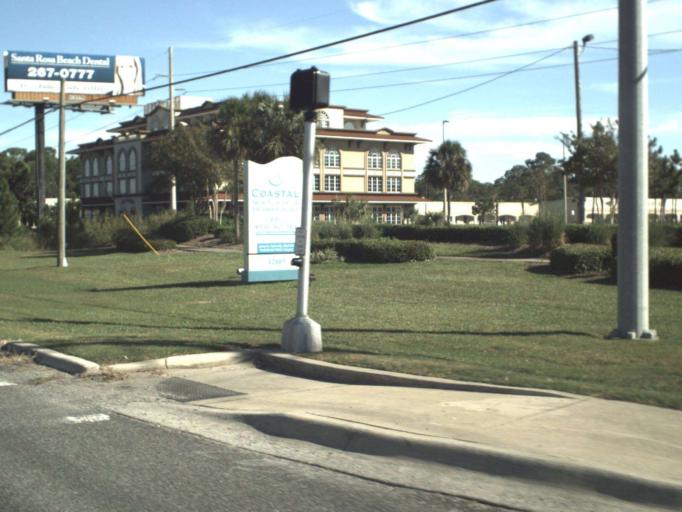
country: US
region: Florida
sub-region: Walton County
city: Miramar Beach
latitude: 30.3850
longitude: -86.3803
